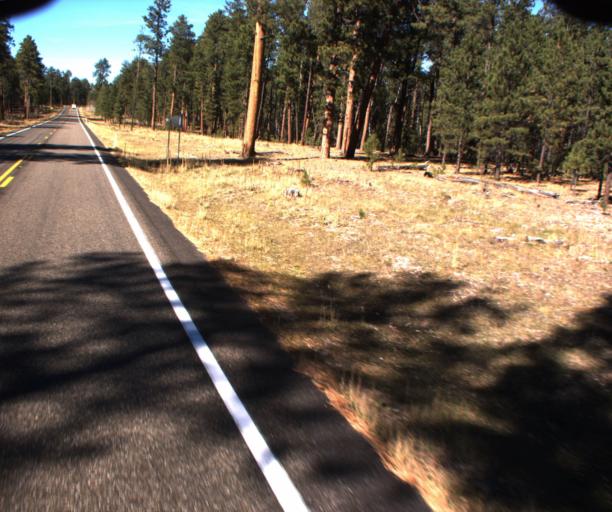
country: US
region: Arizona
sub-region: Coconino County
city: Fredonia
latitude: 36.6534
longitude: -112.1854
